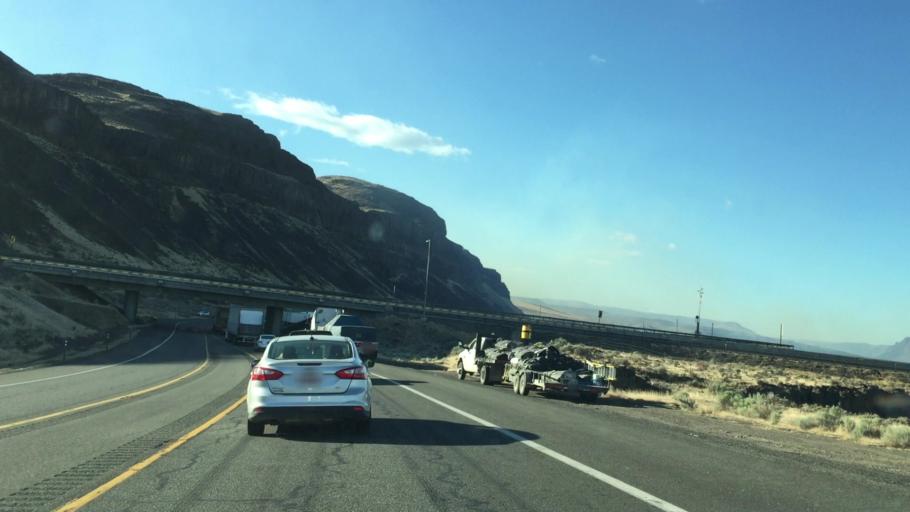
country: US
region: Washington
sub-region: Grant County
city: Mattawa
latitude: 46.9460
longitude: -119.9632
